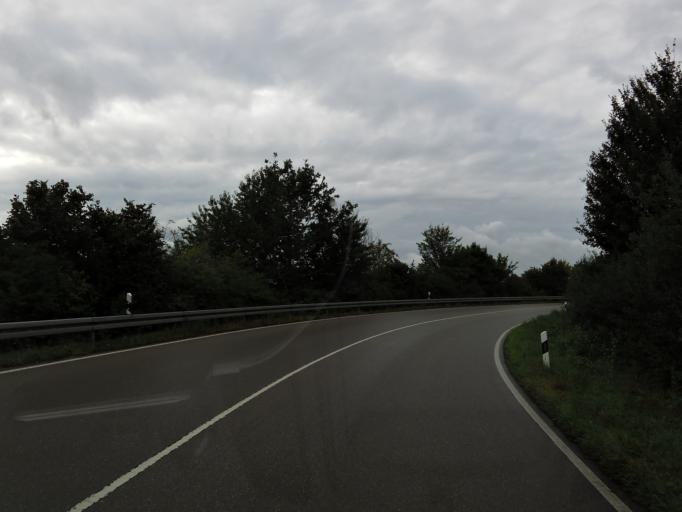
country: DE
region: Bavaria
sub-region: Upper Bavaria
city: Stammham
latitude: 48.3189
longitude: 11.8818
